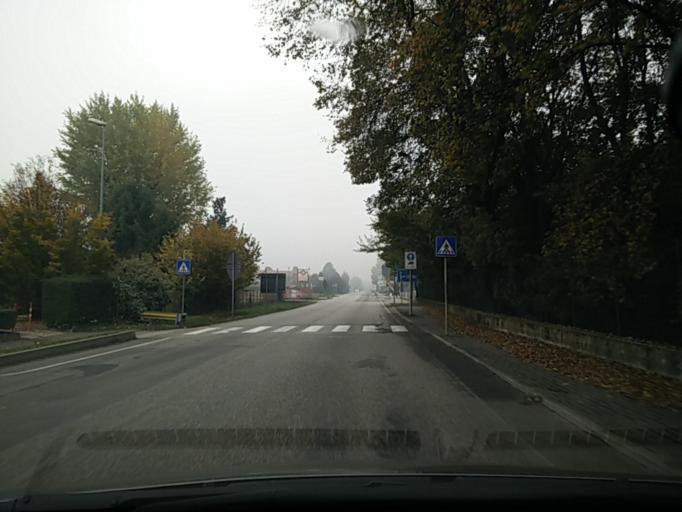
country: IT
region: Veneto
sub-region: Provincia di Venezia
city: Maerne
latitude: 45.5177
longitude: 12.1512
